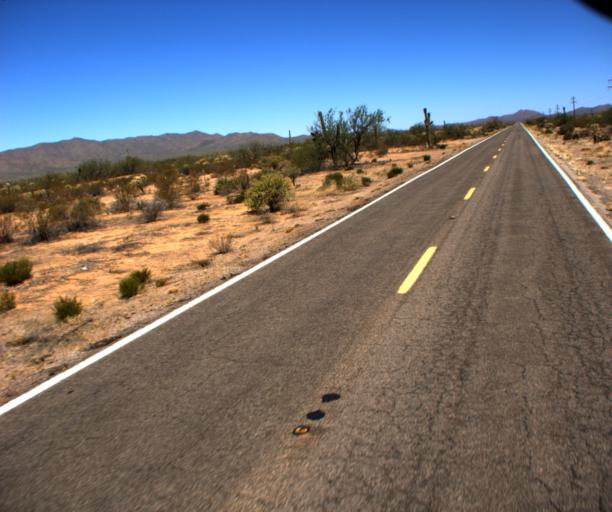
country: US
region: Arizona
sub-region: Pima County
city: Sells
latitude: 32.0974
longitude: -112.0633
